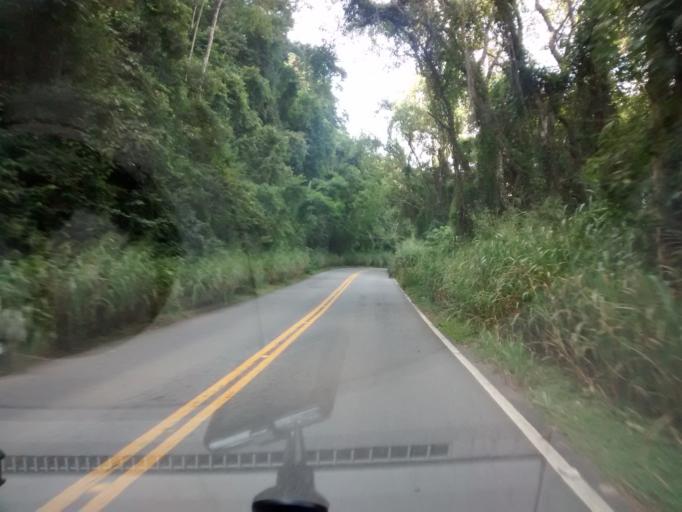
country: BR
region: Rio de Janeiro
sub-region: Miguel Pereira
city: Miguel Pereira
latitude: -22.4715
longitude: -43.5434
